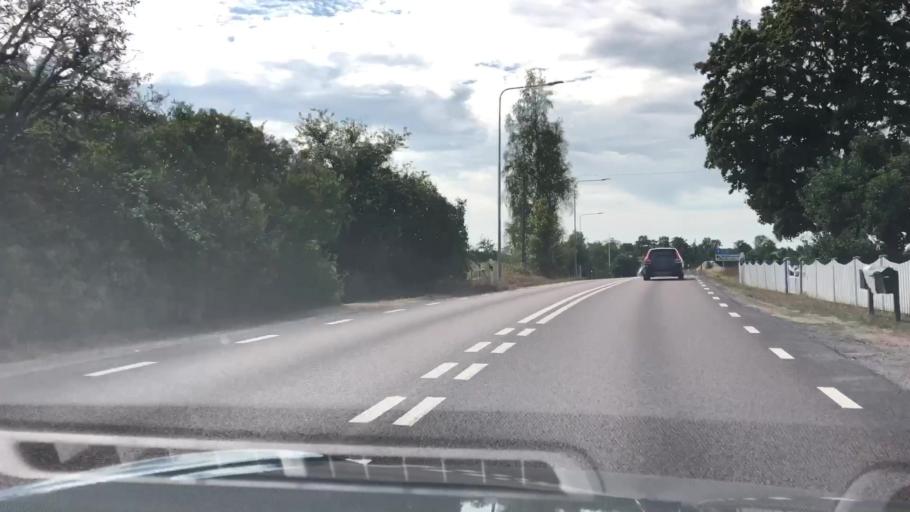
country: SE
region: Kalmar
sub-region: Torsas Kommun
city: Torsas
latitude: 56.3786
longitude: 16.0701
